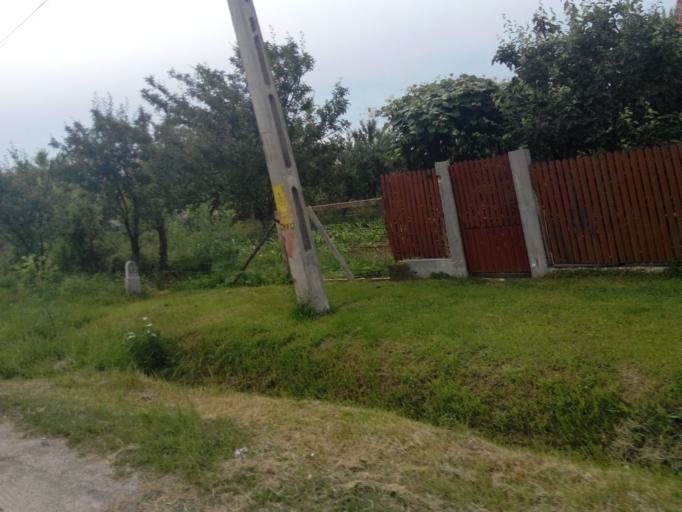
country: RO
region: Arges
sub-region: Comuna Bascov
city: Bascov
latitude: 44.9161
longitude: 24.8018
